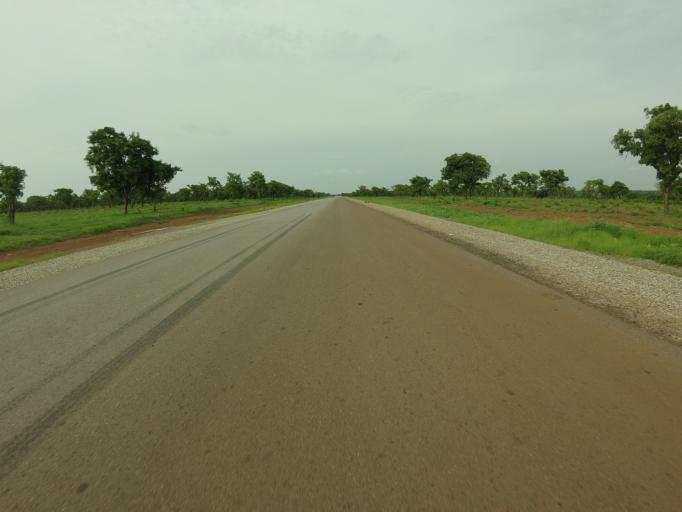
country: GH
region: Northern
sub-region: Yendi
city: Yendi
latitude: 9.7834
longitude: -0.1164
